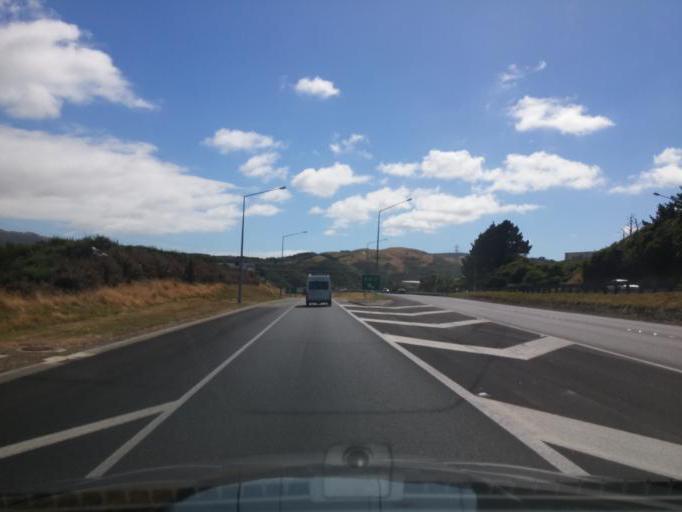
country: NZ
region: Wellington
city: Petone
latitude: -41.1885
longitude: 174.8313
